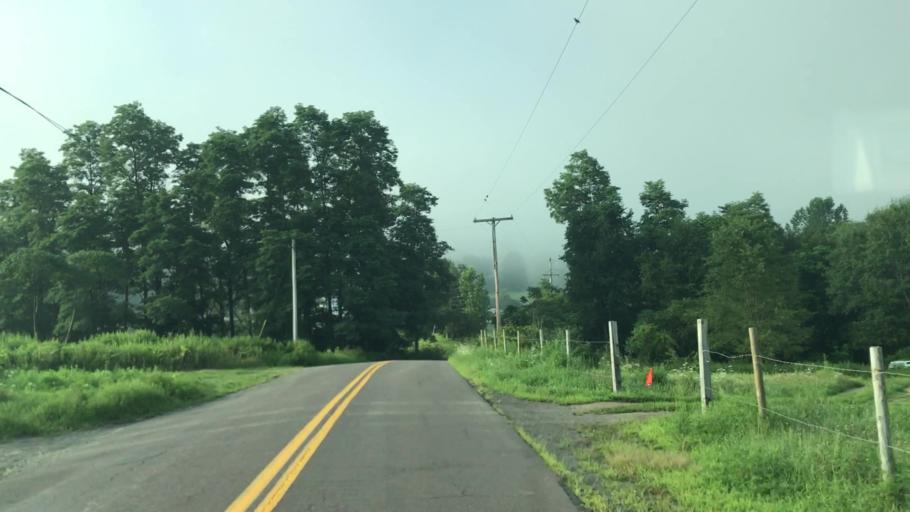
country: US
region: Pennsylvania
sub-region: Wyoming County
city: Factoryville
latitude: 41.6222
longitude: -75.7686
